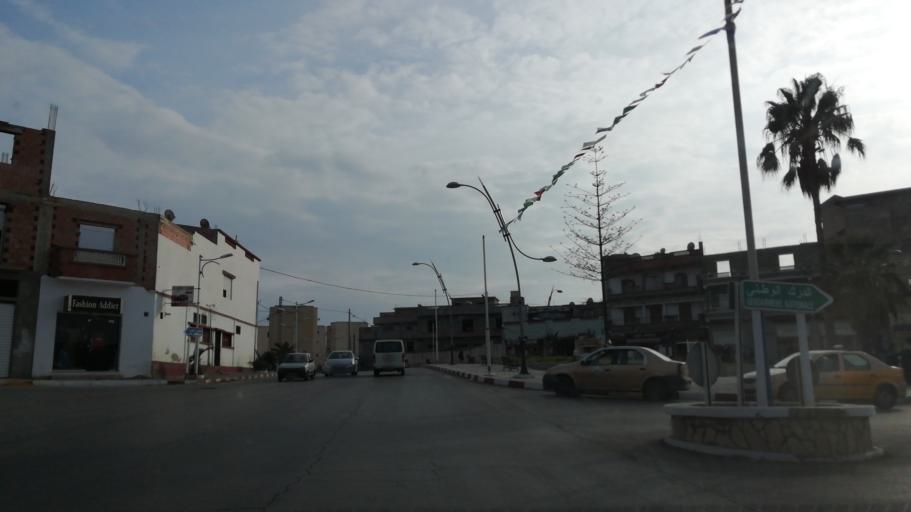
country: DZ
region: Mostaganem
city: Mostaganem
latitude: 35.8976
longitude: 0.0740
